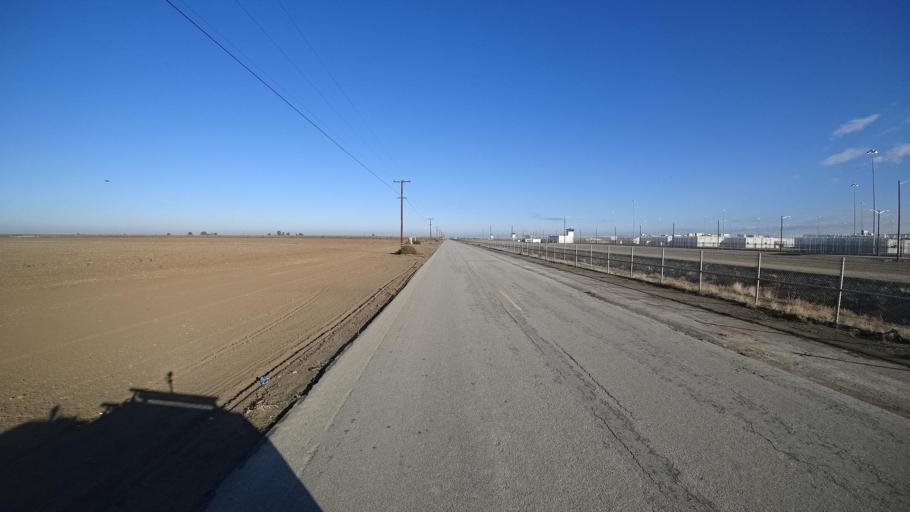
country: US
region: California
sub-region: Kern County
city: Delano
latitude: 35.7641
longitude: -119.3297
